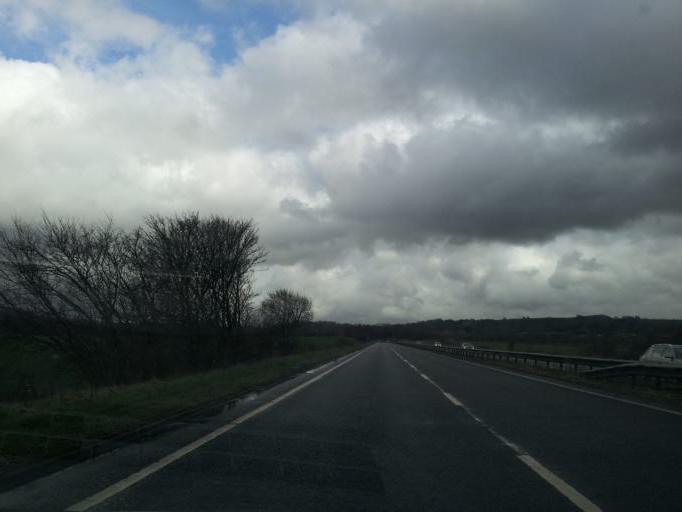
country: GB
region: England
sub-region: Somerset
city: Castle Cary
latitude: 51.0358
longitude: -2.5426
